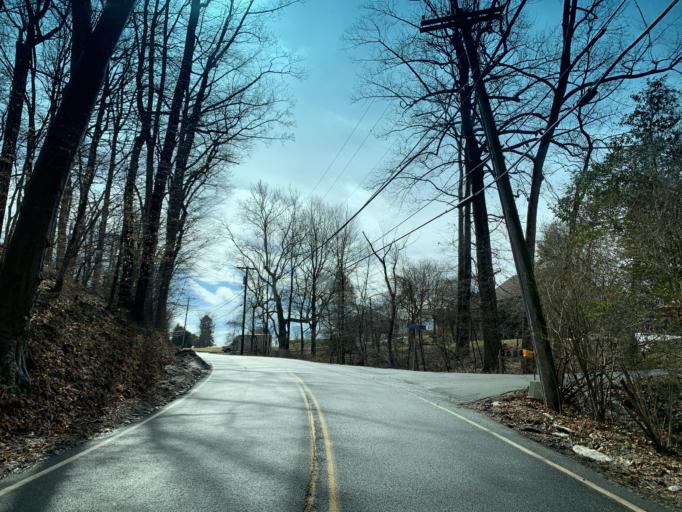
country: US
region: Delaware
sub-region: New Castle County
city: Newark
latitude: 39.7001
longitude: -75.8003
